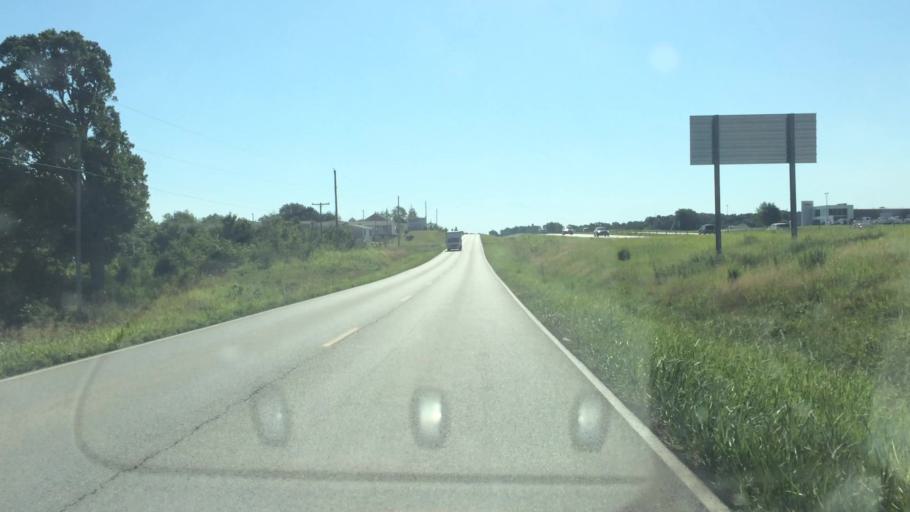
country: US
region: Missouri
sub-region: Greene County
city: Strafford
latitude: 37.2709
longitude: -93.0858
